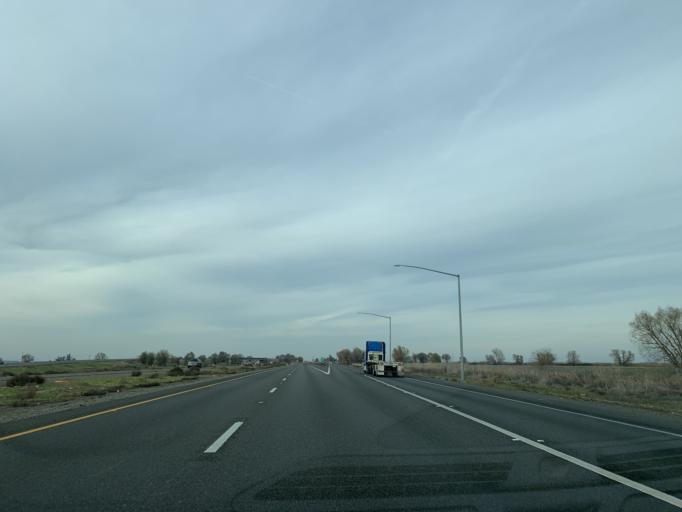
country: US
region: California
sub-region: Sacramento County
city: Elverta
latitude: 38.8453
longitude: -121.5435
